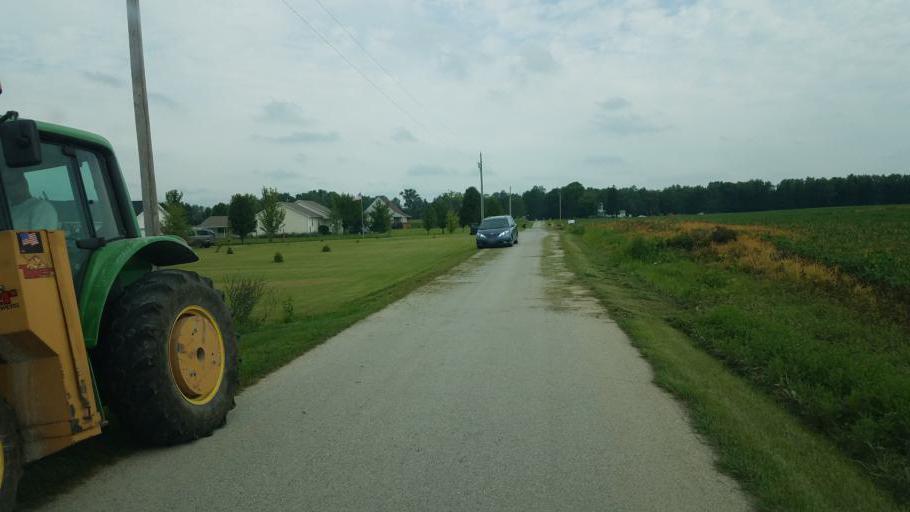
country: US
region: Ohio
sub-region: Morrow County
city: Cardington
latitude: 40.5085
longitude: -82.9391
